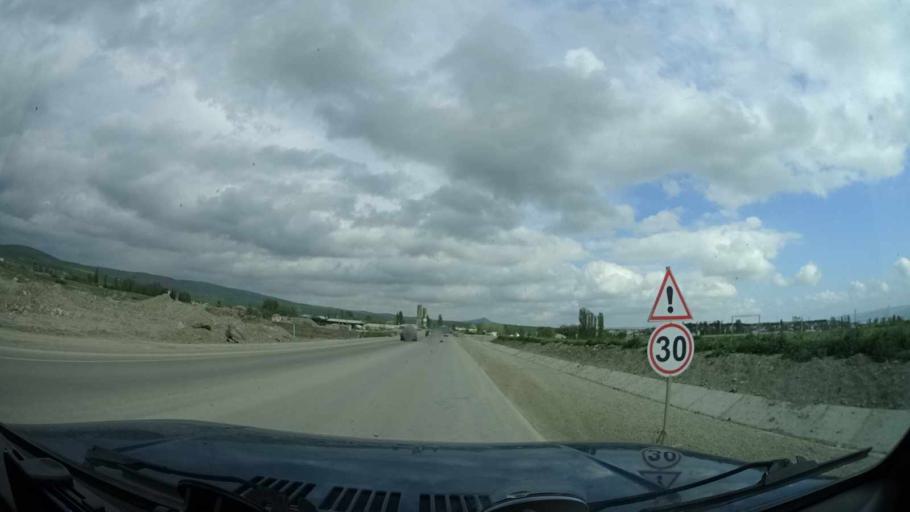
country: AZ
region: Samaxi
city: Shamakhi
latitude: 40.5959
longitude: 48.6981
